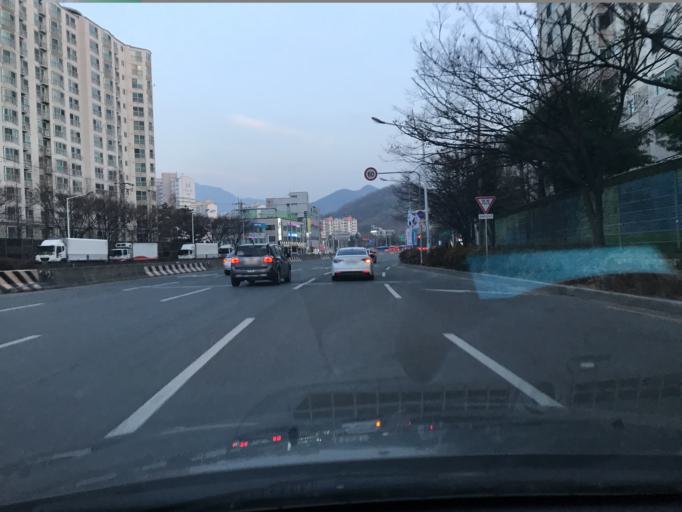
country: KR
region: Daegu
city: Hwawon
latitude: 35.8100
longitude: 128.5166
